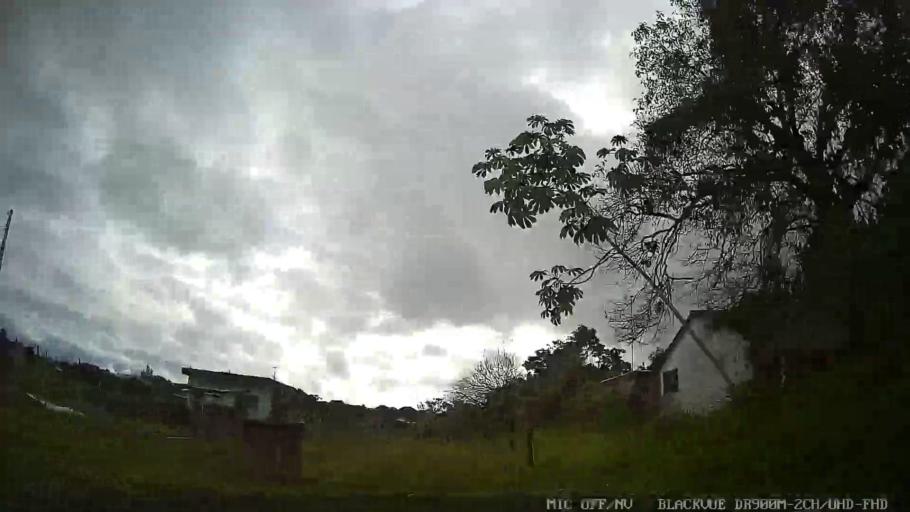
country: BR
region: Sao Paulo
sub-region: Itanhaem
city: Itanhaem
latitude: -24.2207
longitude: -46.8827
